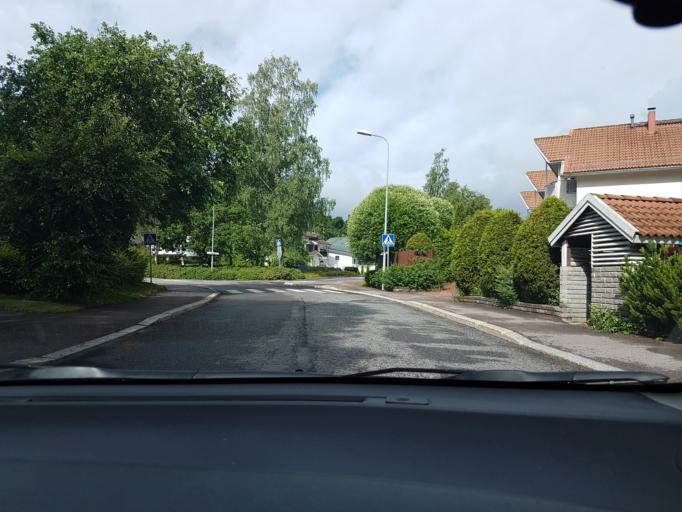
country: FI
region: Uusimaa
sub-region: Helsinki
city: Vantaa
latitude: 60.2185
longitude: 25.1153
